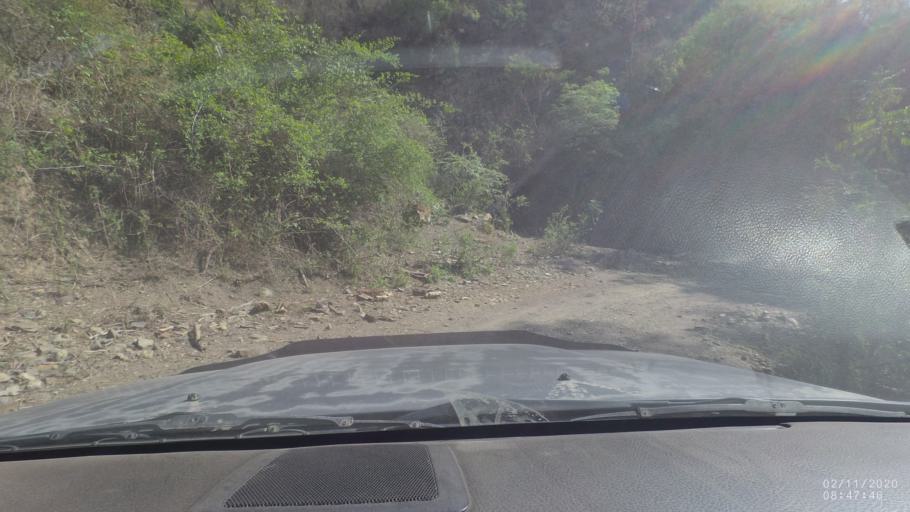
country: BO
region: Chuquisaca
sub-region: Provincia Zudanez
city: Mojocoya
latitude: -18.5598
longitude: -64.5476
